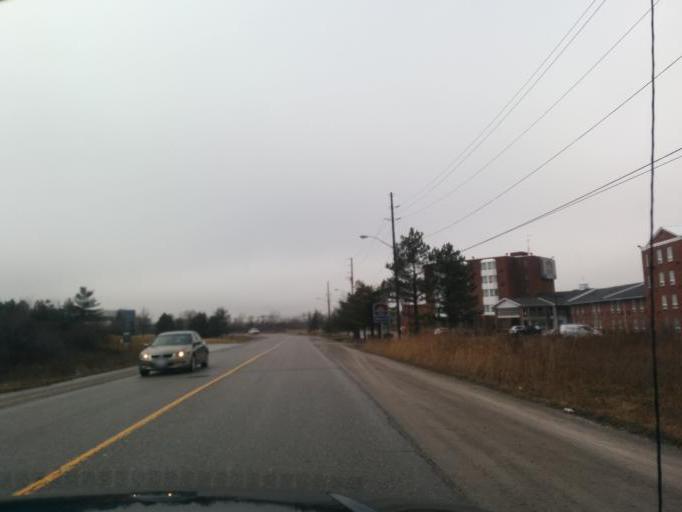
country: CA
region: Ontario
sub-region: Halton
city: Milton
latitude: 43.5251
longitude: -79.9067
